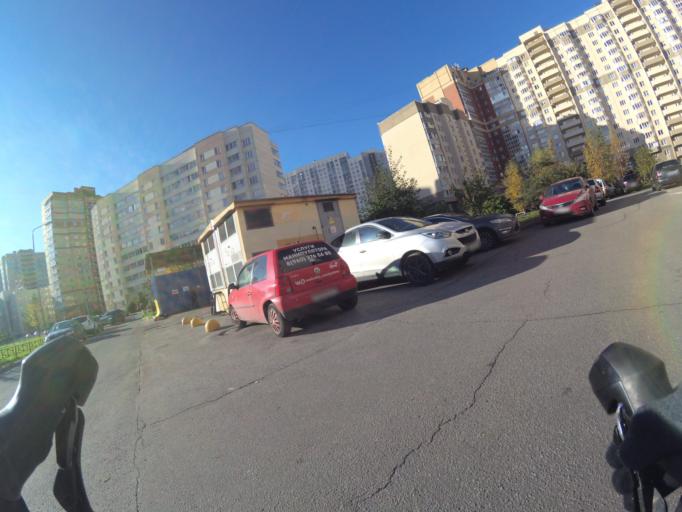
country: RU
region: Leningrad
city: Untolovo
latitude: 59.9997
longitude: 30.2030
